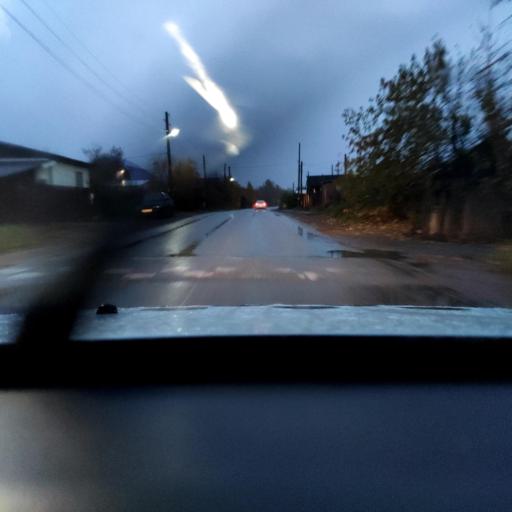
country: RU
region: Perm
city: Kondratovo
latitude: 57.9865
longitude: 56.1000
